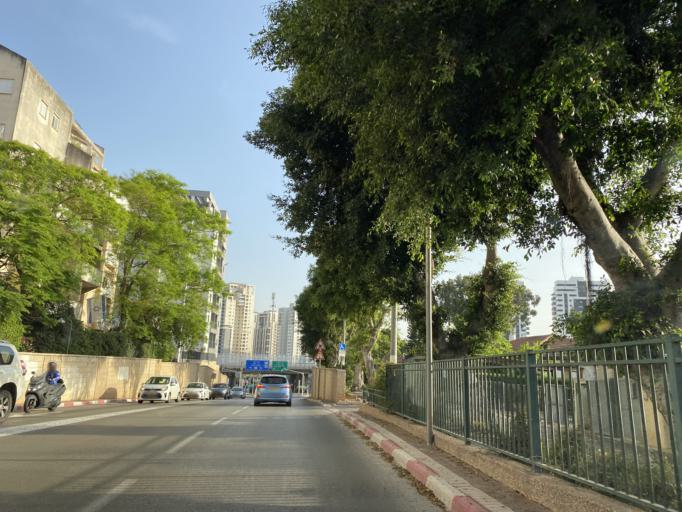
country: IL
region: Central District
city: Kfar Saba
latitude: 32.1723
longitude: 34.9014
